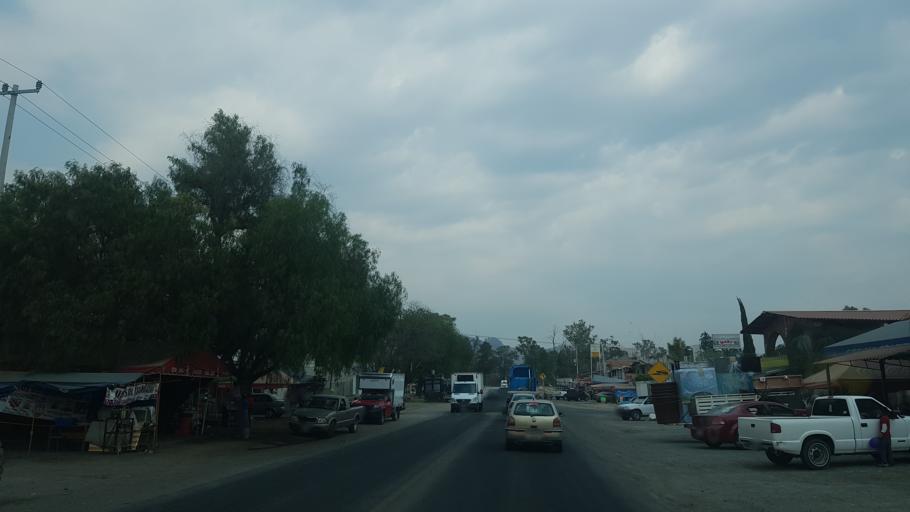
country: MX
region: Puebla
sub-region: Santa Isabel Cholula
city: Santa Ana Acozautla
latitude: 18.9437
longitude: -98.3942
